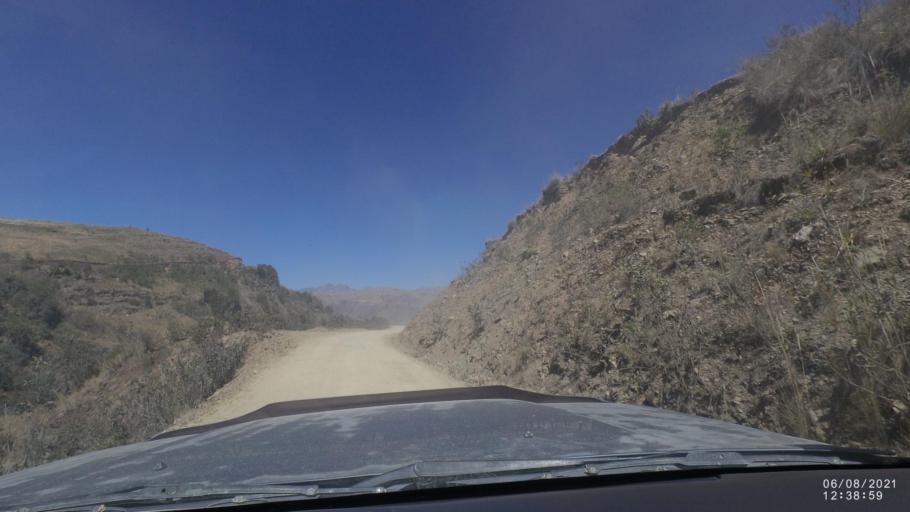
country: BO
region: Cochabamba
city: Colchani
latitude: -16.7772
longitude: -66.6622
